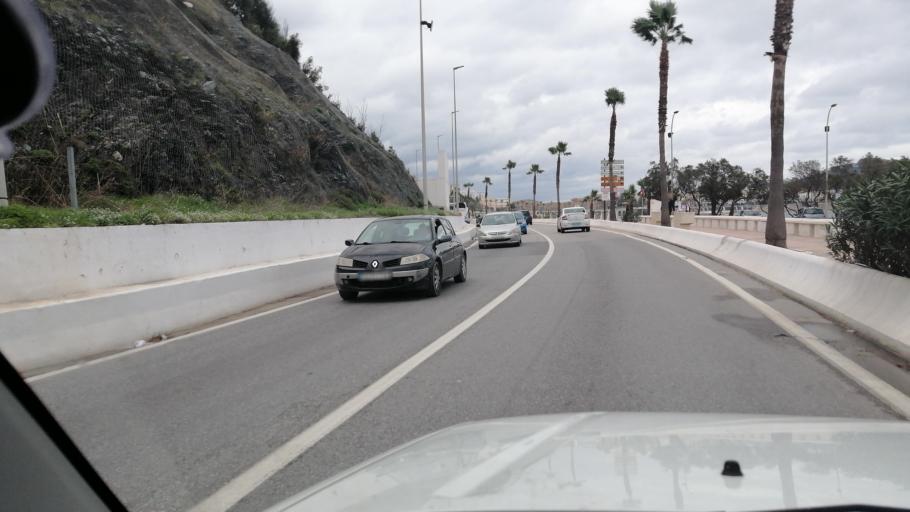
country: ES
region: Ceuta
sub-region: Ceuta
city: Ceuta
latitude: 35.8814
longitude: -5.3257
